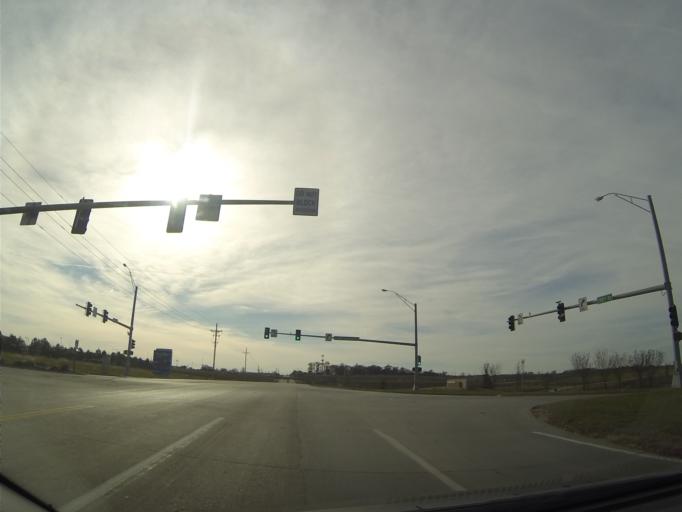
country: US
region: Nebraska
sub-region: Douglas County
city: Elkhorn
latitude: 41.2668
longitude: -96.2156
